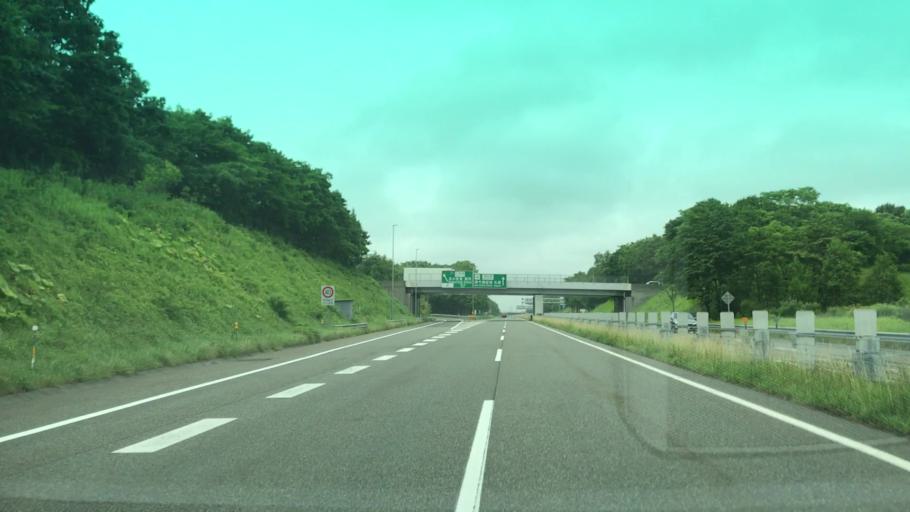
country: JP
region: Hokkaido
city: Tomakomai
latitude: 42.7084
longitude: 141.6519
